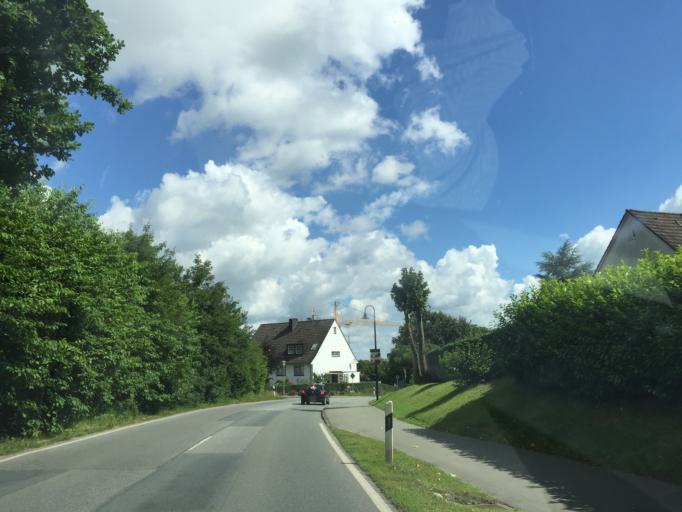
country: DE
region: Schleswig-Holstein
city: Scharbeutz
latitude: 54.0183
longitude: 10.7400
